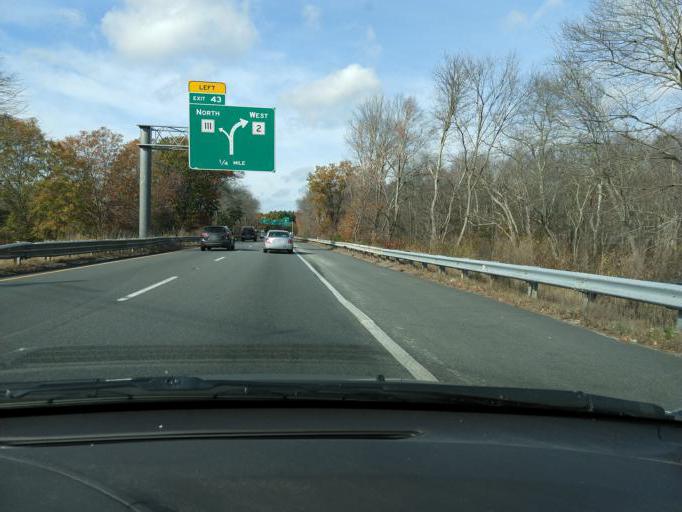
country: US
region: Massachusetts
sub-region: Middlesex County
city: Acton
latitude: 42.4732
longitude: -71.4408
